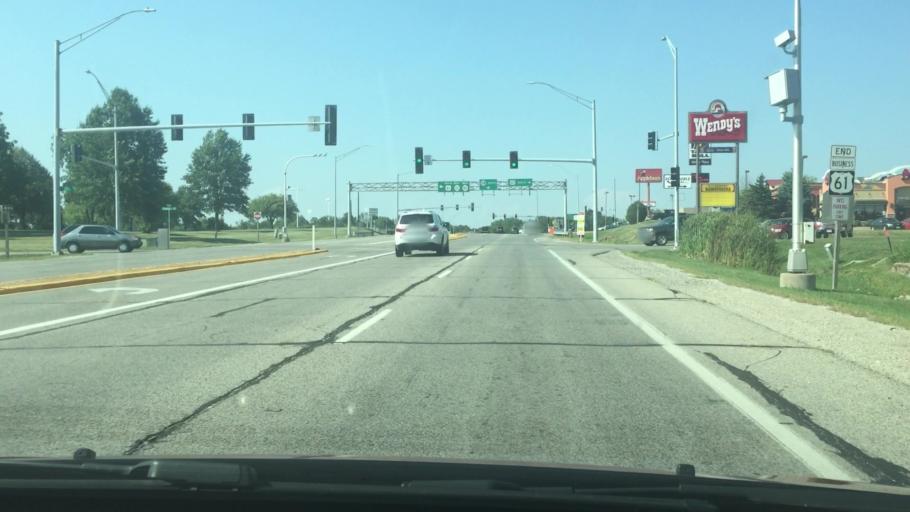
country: US
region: Iowa
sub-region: Muscatine County
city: Muscatine
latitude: 41.4514
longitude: -91.0301
